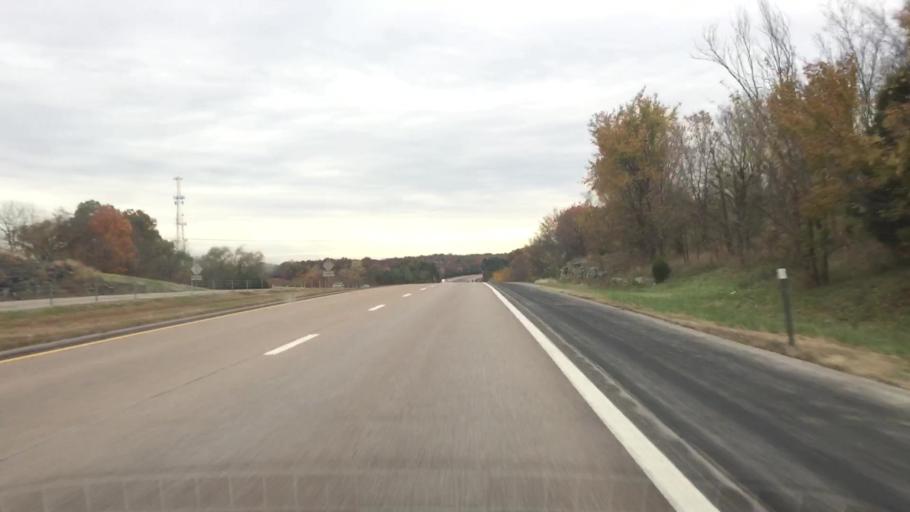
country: US
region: Missouri
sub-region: Boone County
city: Ashland
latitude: 38.6739
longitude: -92.2405
